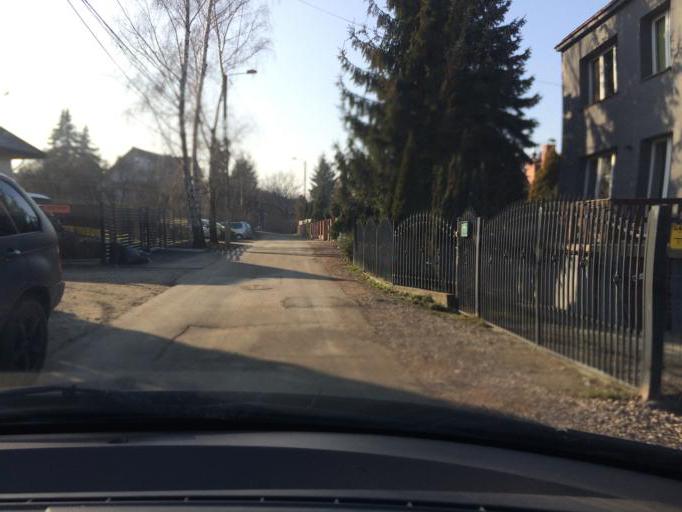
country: PL
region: Lesser Poland Voivodeship
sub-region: Powiat wielicki
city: Czarnochowice
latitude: 50.0040
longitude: 20.0406
